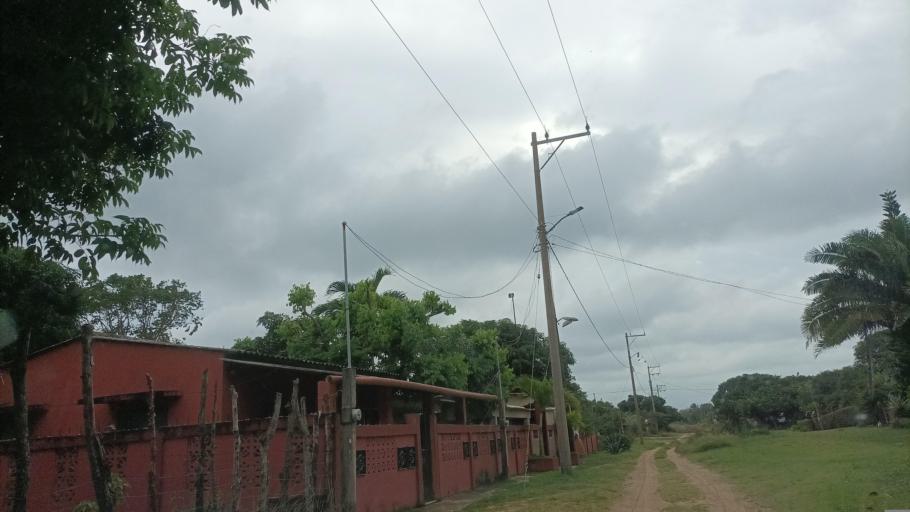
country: MX
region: Veracruz
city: Agua Dulce
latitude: 18.2070
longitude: -94.1446
